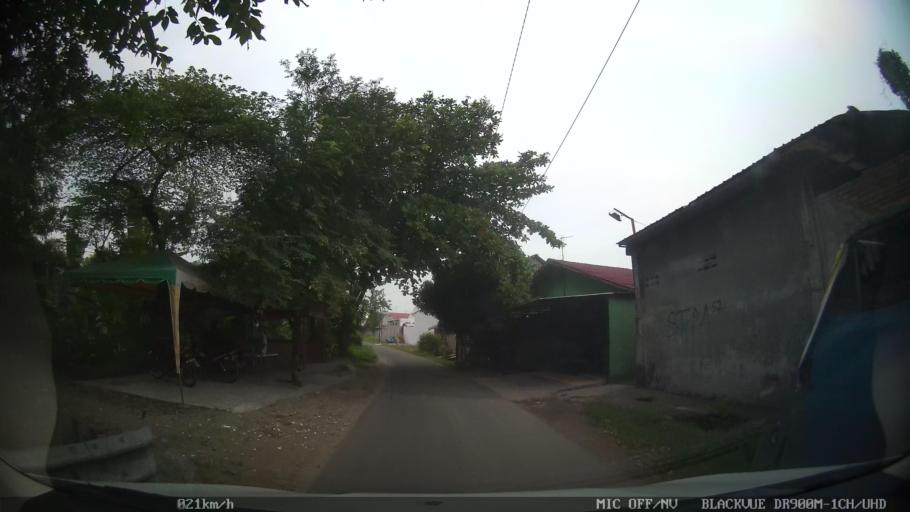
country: ID
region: North Sumatra
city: Deli Tua
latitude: 3.5487
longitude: 98.7137
